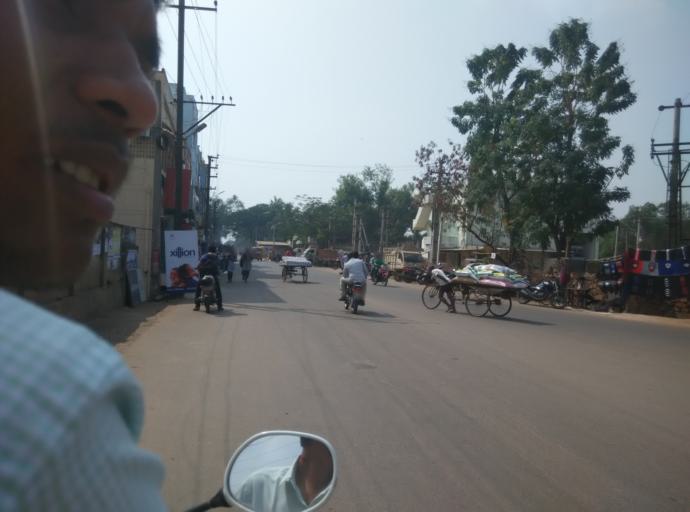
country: IN
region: Andhra Pradesh
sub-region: Vizianagaram District
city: Vizianagaram
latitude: 18.1141
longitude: 83.4090
